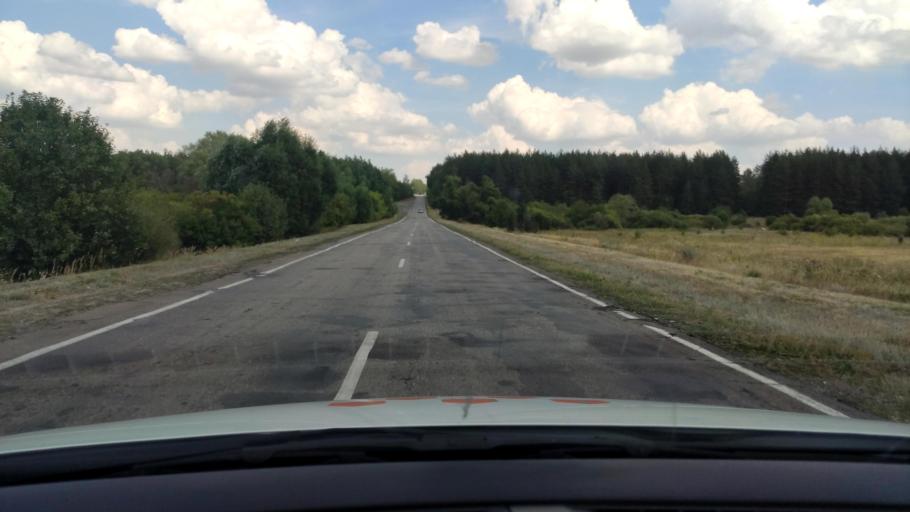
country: RU
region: Voronezj
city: Sadovoye
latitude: 51.7781
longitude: 40.5297
